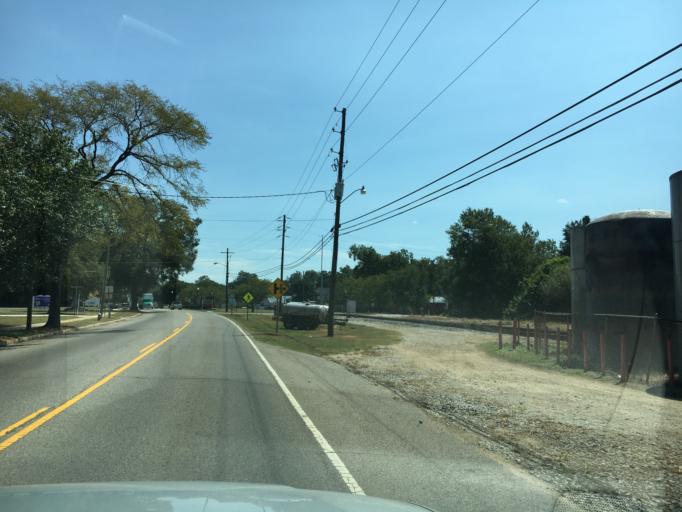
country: US
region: South Carolina
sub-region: Lexington County
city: Batesburg
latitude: 33.8458
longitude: -81.6646
